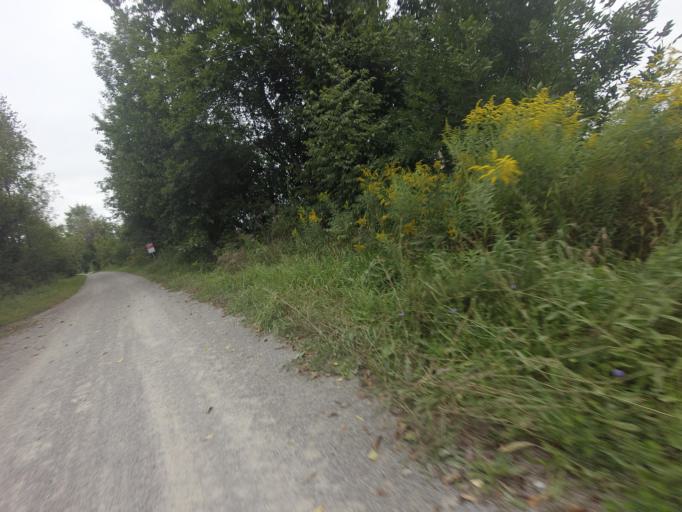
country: CA
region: Ontario
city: Omemee
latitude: 44.4005
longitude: -78.7588
